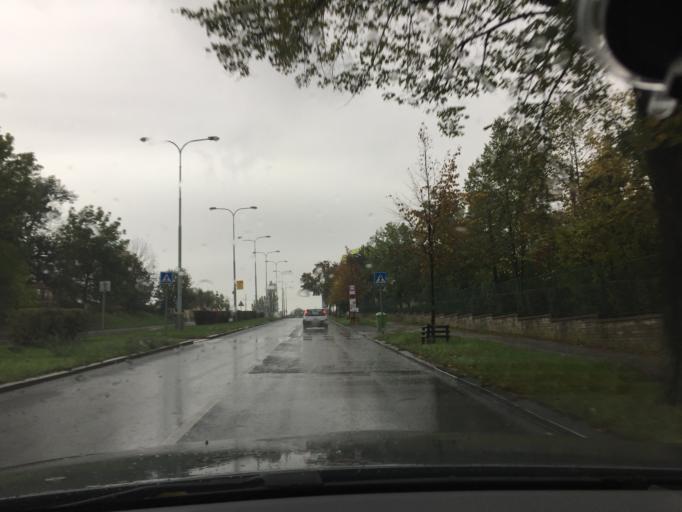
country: CZ
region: Praha
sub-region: Praha 8
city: Liben
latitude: 50.1310
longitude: 14.4526
